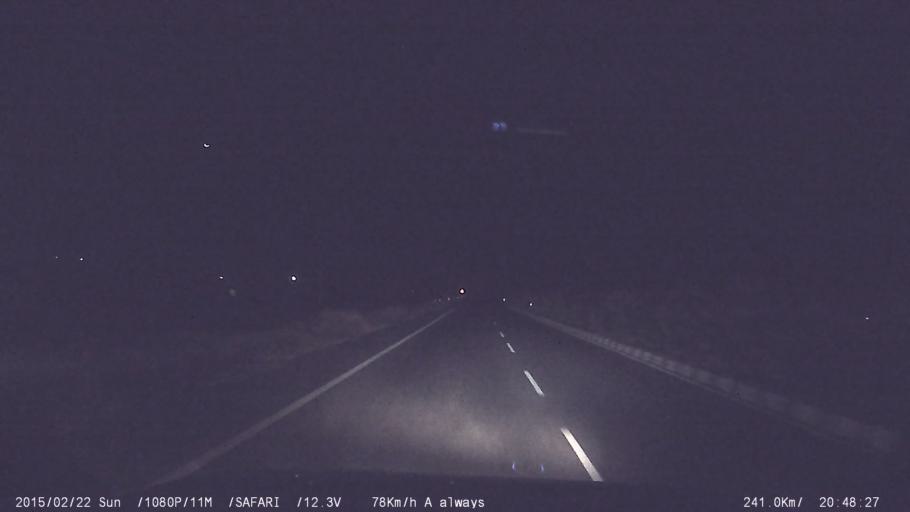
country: IN
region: Tamil Nadu
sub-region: Dindigul
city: Vedasandur
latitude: 10.5073
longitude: 77.9413
